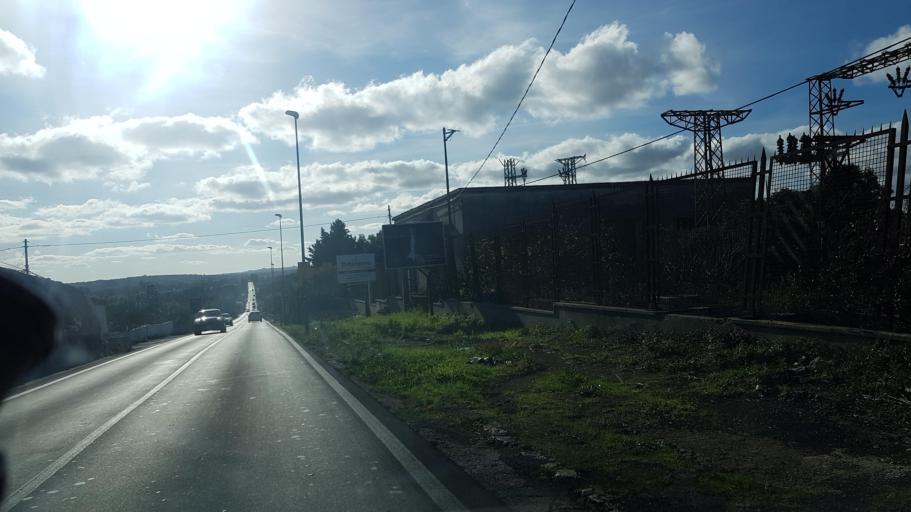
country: IT
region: Apulia
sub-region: Provincia di Brindisi
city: Ostuni
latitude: 40.7169
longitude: 17.5737
